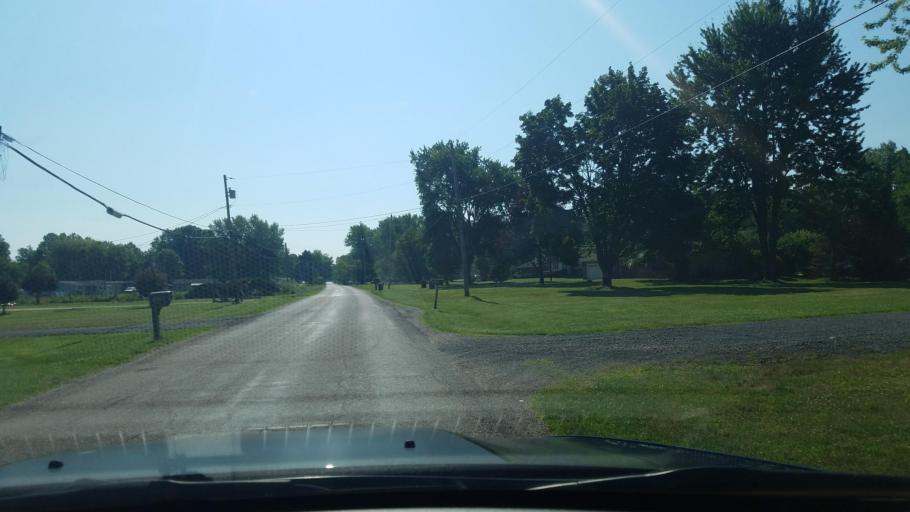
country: US
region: Ohio
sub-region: Trumbull County
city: Leavittsburg
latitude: 41.2606
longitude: -80.9228
